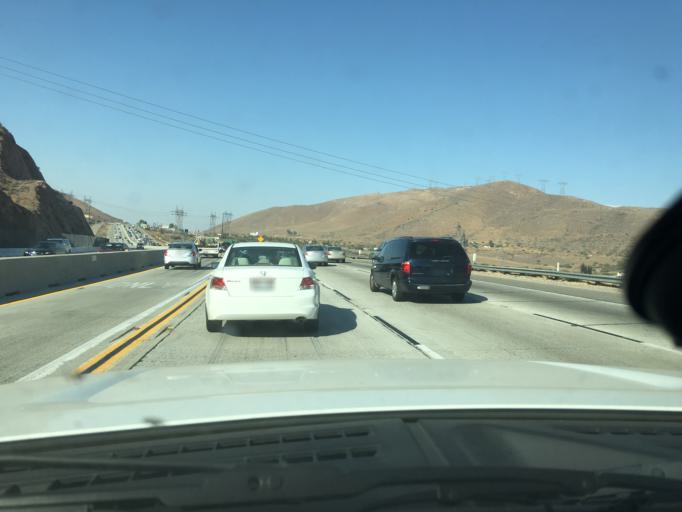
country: US
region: California
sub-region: Los Angeles County
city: Vincent
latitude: 34.4923
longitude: -118.1278
